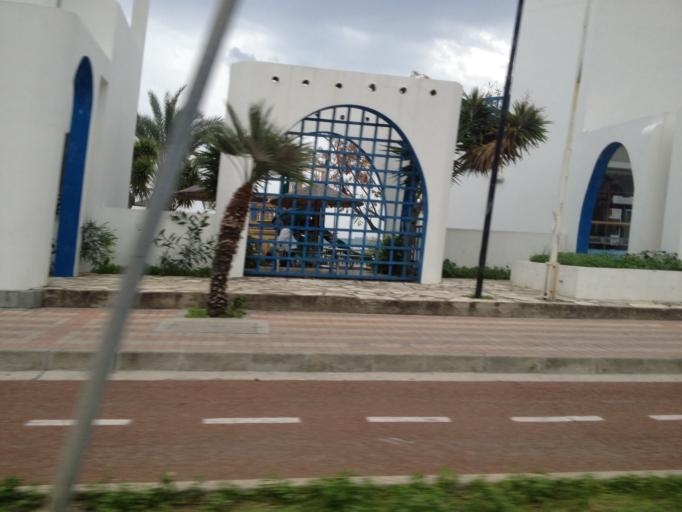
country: CY
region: Limassol
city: Limassol
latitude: 34.6895
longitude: 33.0722
